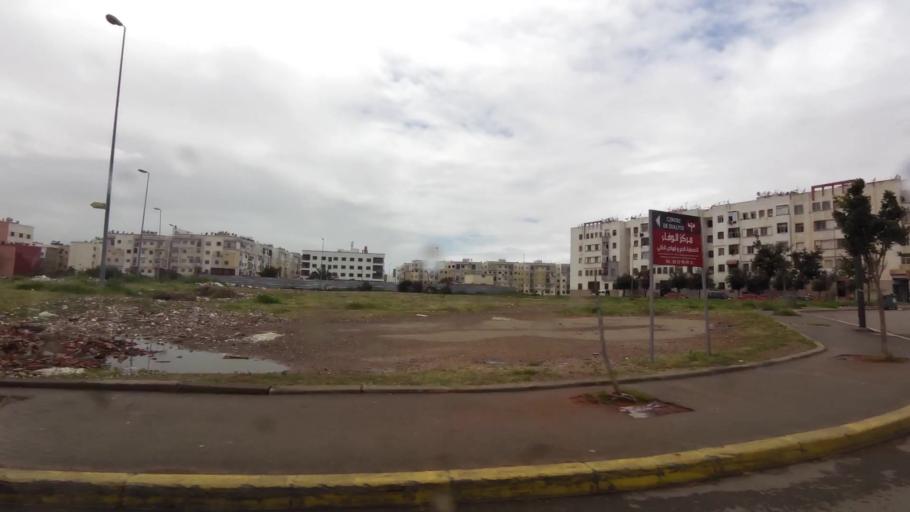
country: MA
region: Grand Casablanca
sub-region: Casablanca
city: Casablanca
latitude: 33.5444
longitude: -7.6855
